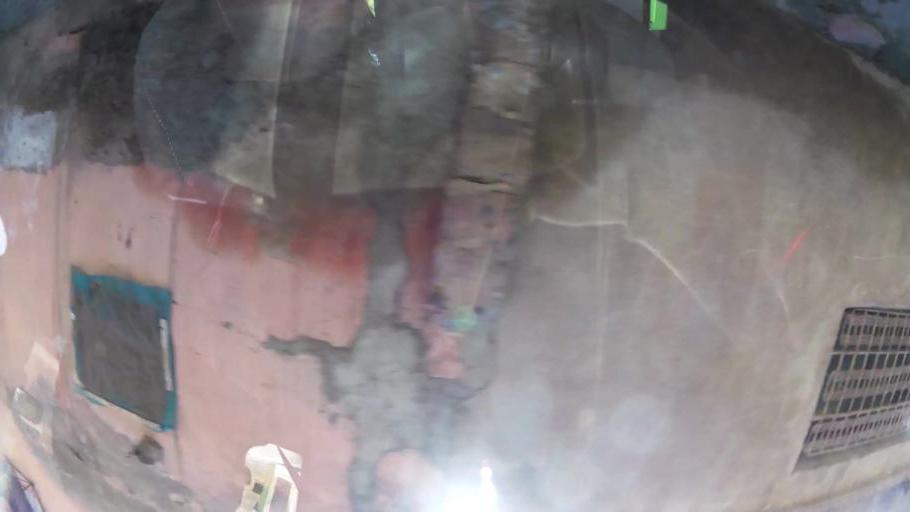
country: MA
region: Marrakech-Tensift-Al Haouz
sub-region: Marrakech
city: Marrakesh
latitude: 31.6386
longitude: -8.0477
